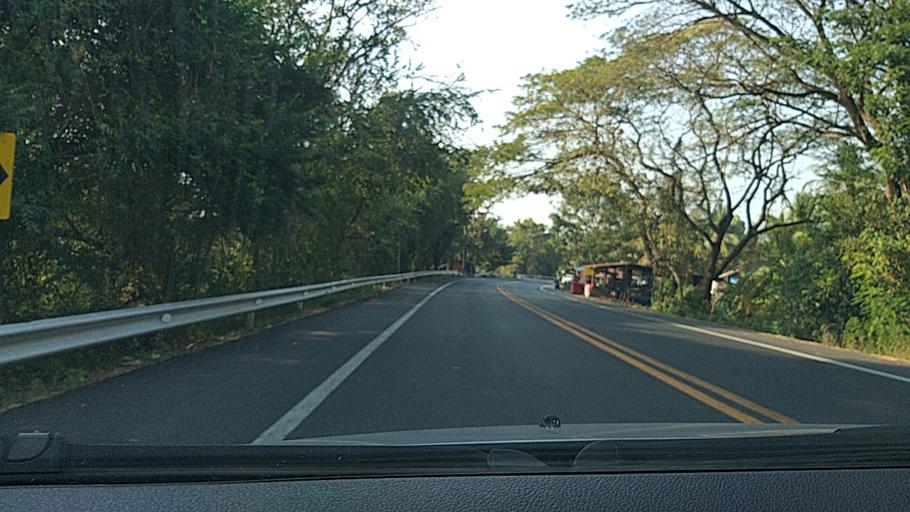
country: TH
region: Sing Buri
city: Phrom Buri
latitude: 14.7554
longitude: 100.4361
